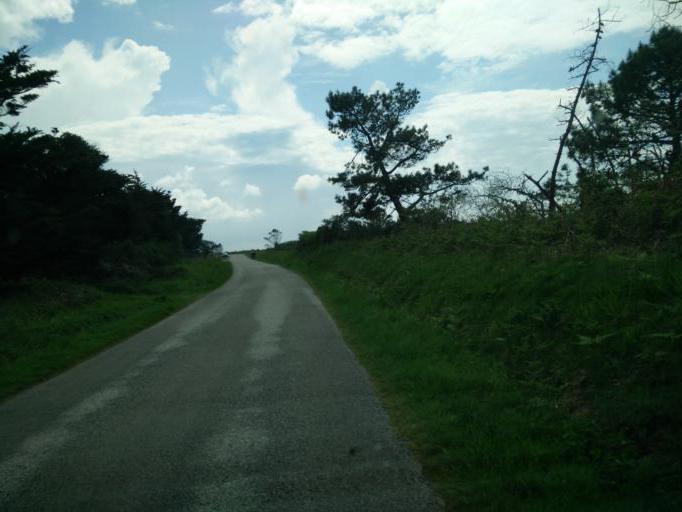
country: FR
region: Brittany
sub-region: Departement du Finistere
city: Roscanvel
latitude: 48.3191
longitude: -4.5755
